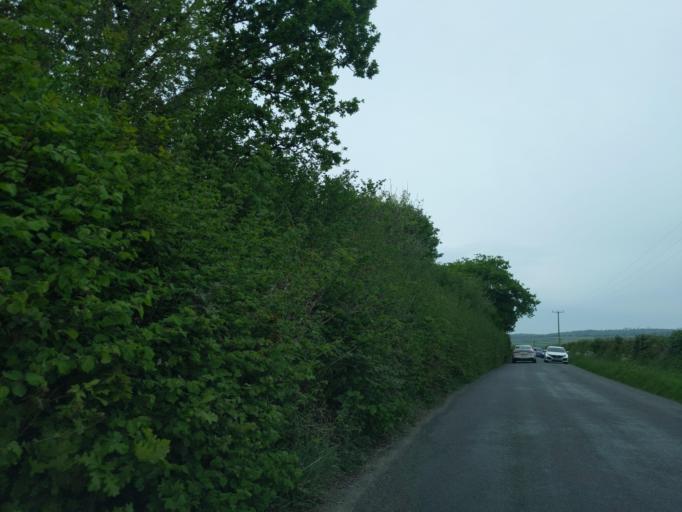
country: GB
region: England
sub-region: Devon
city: Plympton
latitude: 50.4196
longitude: -4.0465
